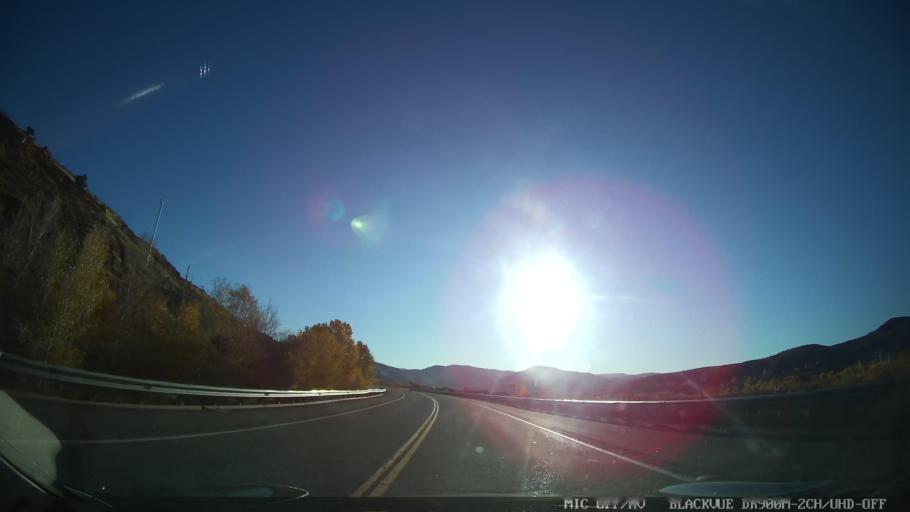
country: US
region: Colorado
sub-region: Grand County
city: Hot Sulphur Springs
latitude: 40.0516
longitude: -106.1697
